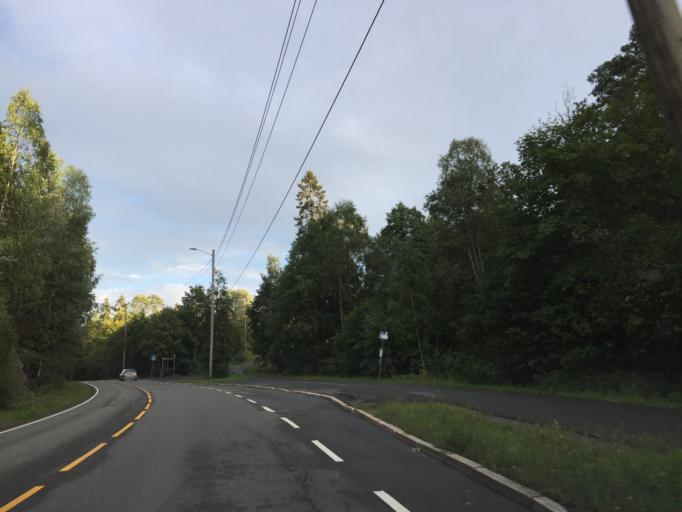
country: NO
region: Akershus
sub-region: Oppegard
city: Kolbotn
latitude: 59.8407
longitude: 10.8275
